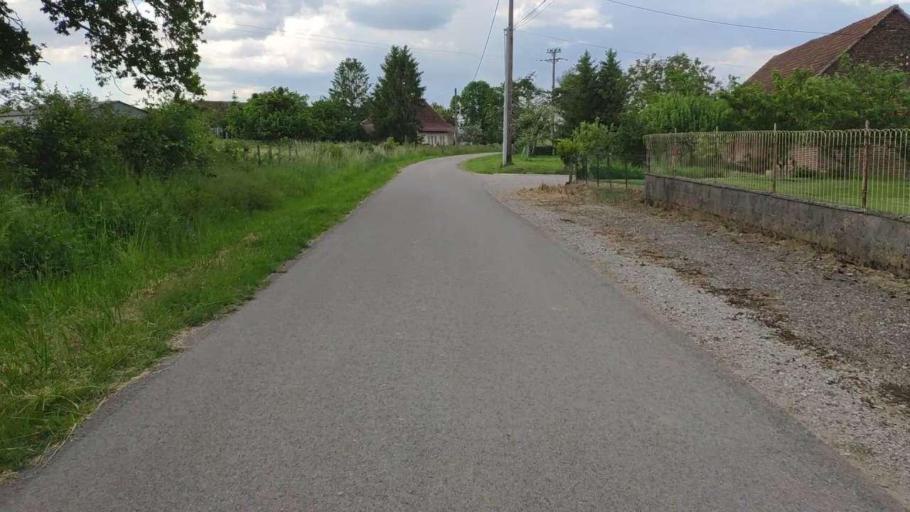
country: FR
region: Franche-Comte
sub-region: Departement du Jura
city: Bletterans
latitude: 46.7972
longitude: 5.3665
